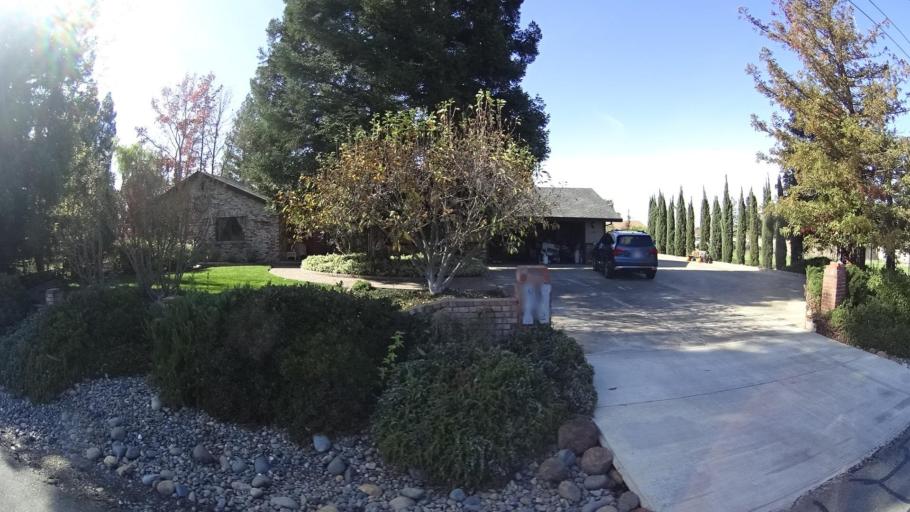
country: US
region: California
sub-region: Sacramento County
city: Elk Grove
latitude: 38.4353
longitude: -121.3669
